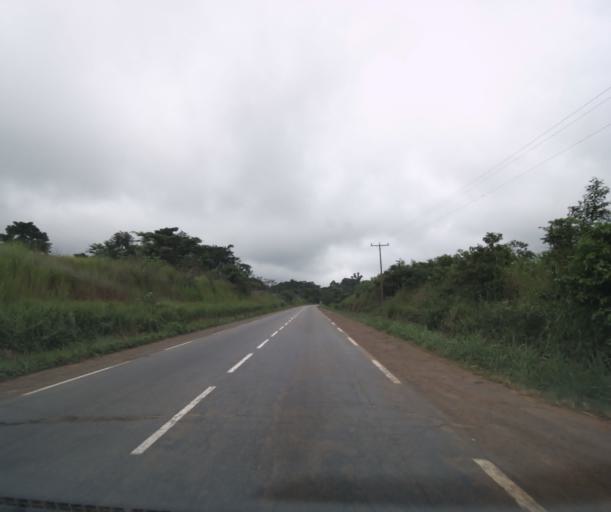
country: CM
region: Centre
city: Mbankomo
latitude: 3.7976
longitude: 11.3608
